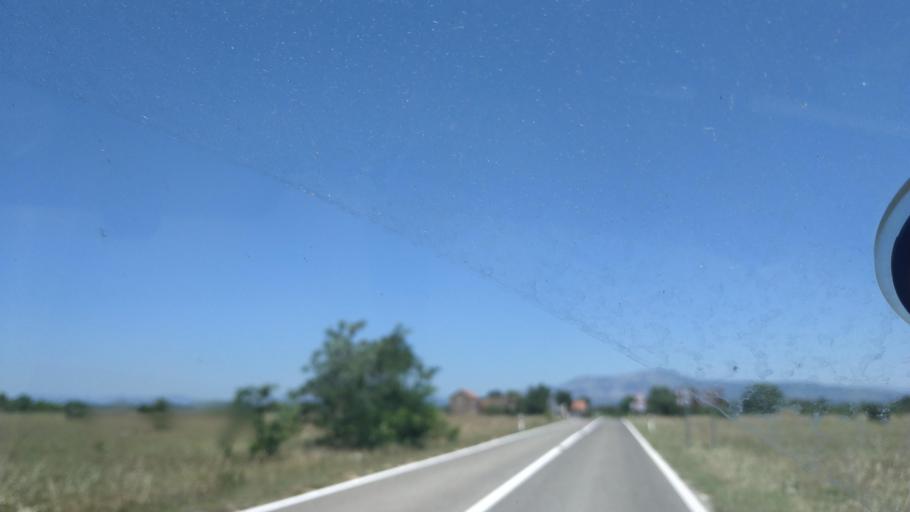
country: HR
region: Sibensko-Kniniska
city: Drnis
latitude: 43.8135
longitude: 16.0515
